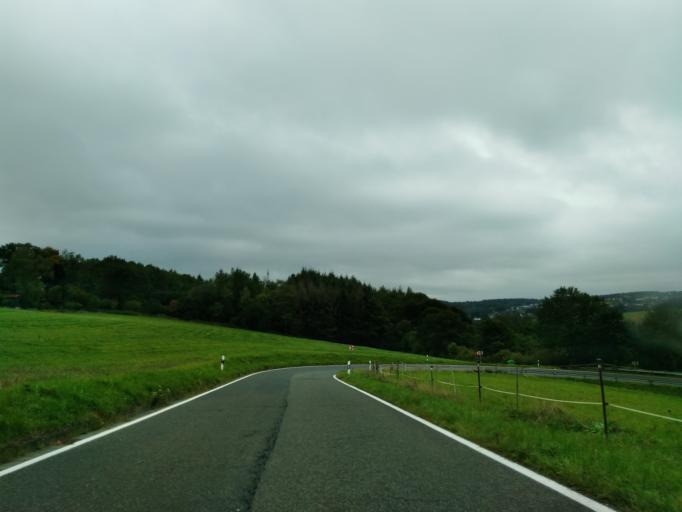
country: DE
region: Rheinland-Pfalz
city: Windhagen
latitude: 50.6346
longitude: 7.3263
